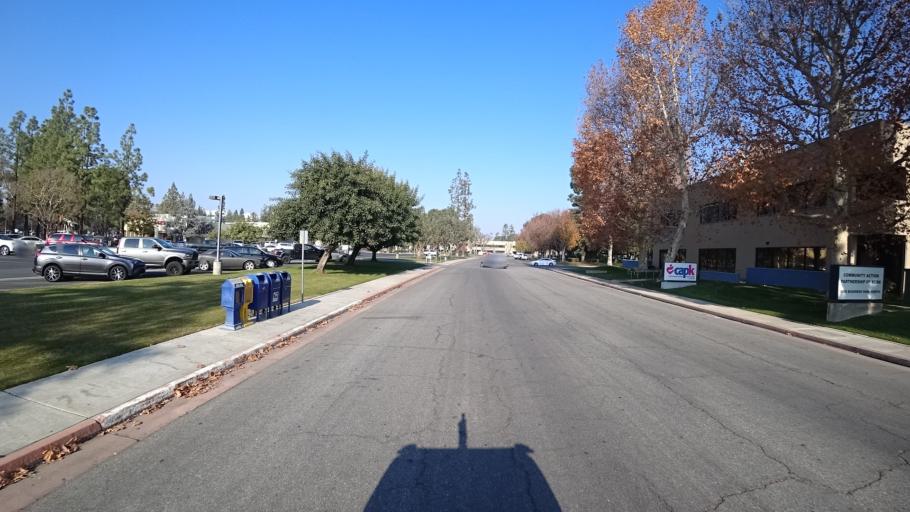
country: US
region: California
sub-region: Kern County
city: Bakersfield
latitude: 35.3610
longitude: -119.0586
